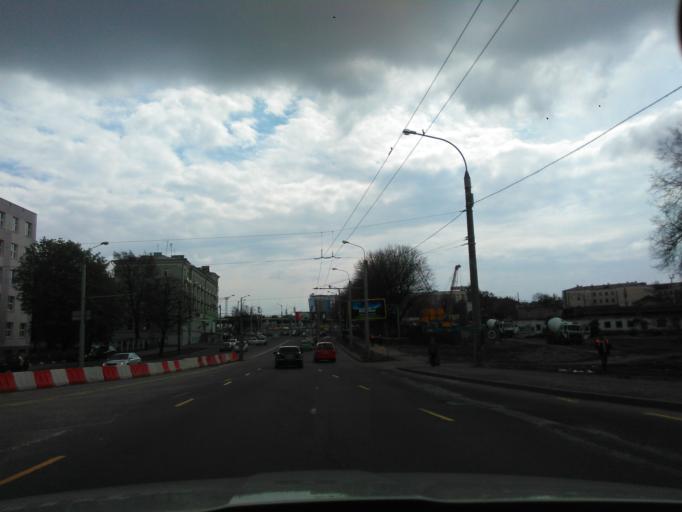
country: BY
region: Minsk
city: Minsk
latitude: 53.8951
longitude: 27.5391
